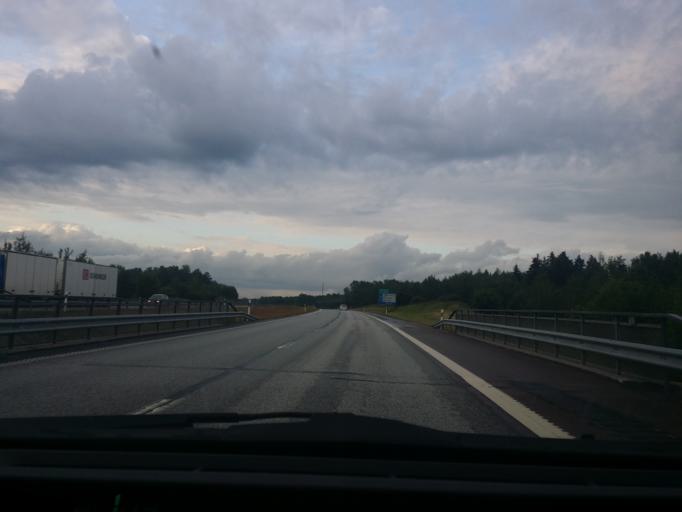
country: SE
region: Vaestmanland
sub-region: Kopings Kommun
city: Koping
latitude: 59.5003
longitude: 15.9329
